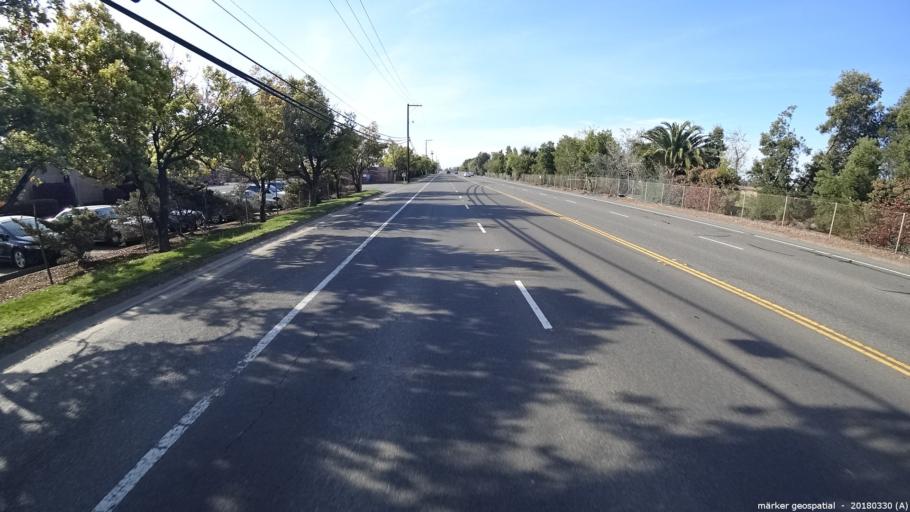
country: US
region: California
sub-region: Sacramento County
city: Rosemont
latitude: 38.5342
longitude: -121.3349
